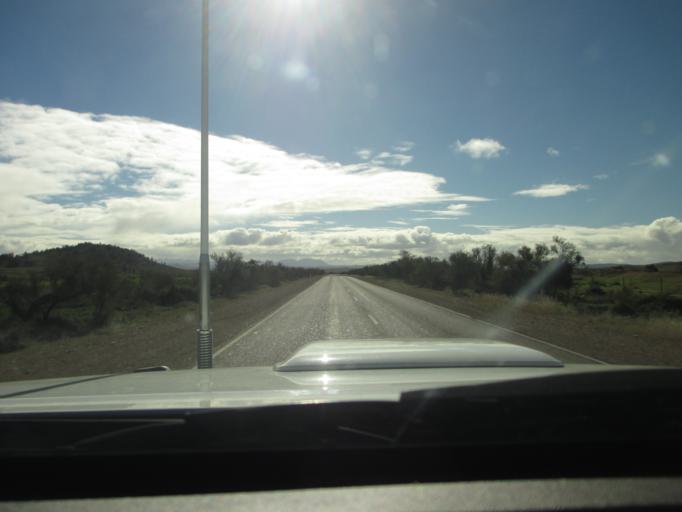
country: AU
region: South Australia
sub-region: Flinders Ranges
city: Quorn
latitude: -31.9200
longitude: 138.4254
